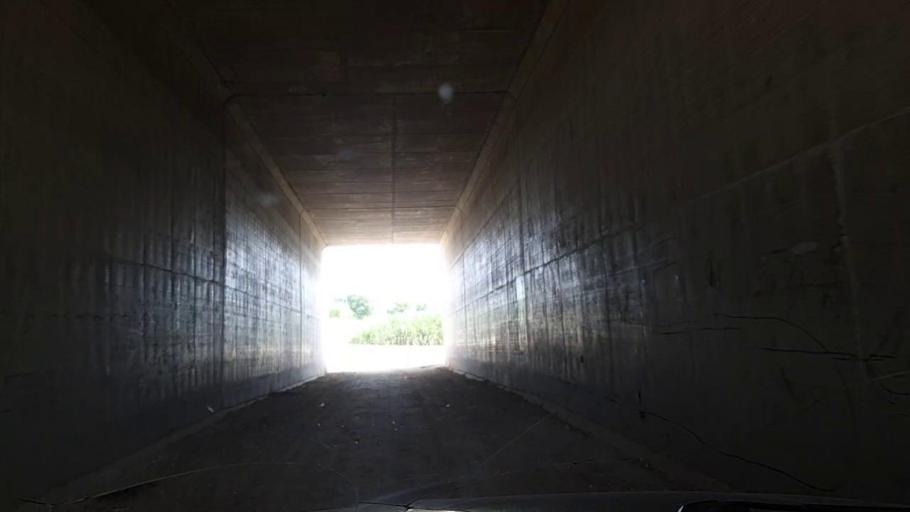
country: PK
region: Sindh
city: Ghotki
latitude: 28.0628
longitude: 69.3816
